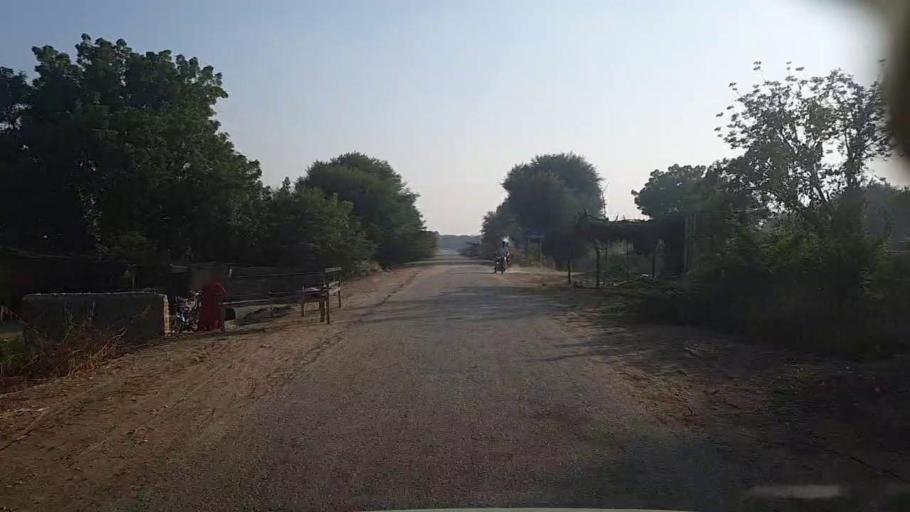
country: PK
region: Sindh
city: Karaundi
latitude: 26.7462
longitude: 68.4769
